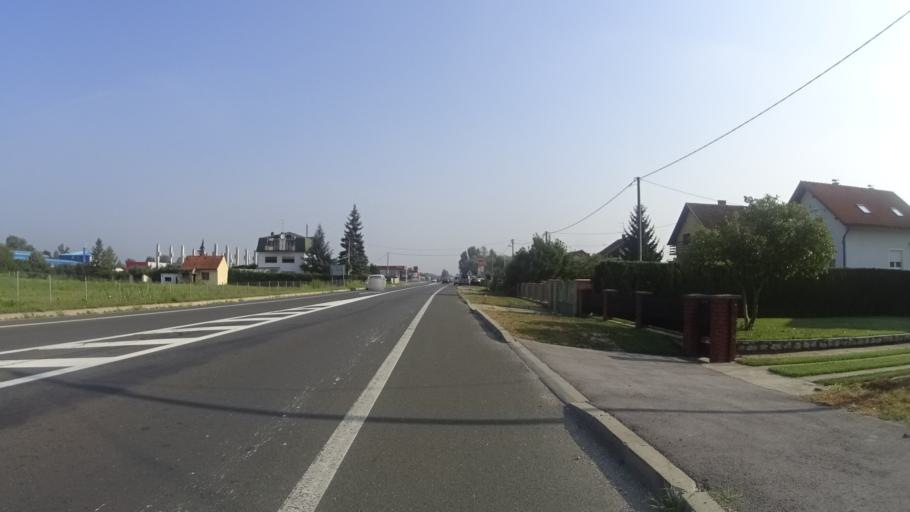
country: HR
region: Varazdinska
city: Varazdin
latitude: 46.3311
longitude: 16.3602
